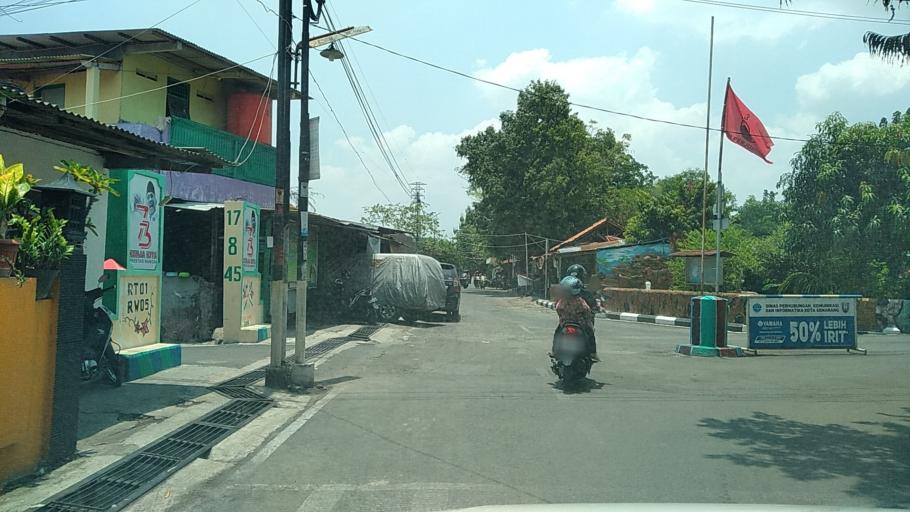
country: ID
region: Central Java
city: Semarang
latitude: -7.0029
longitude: 110.4411
